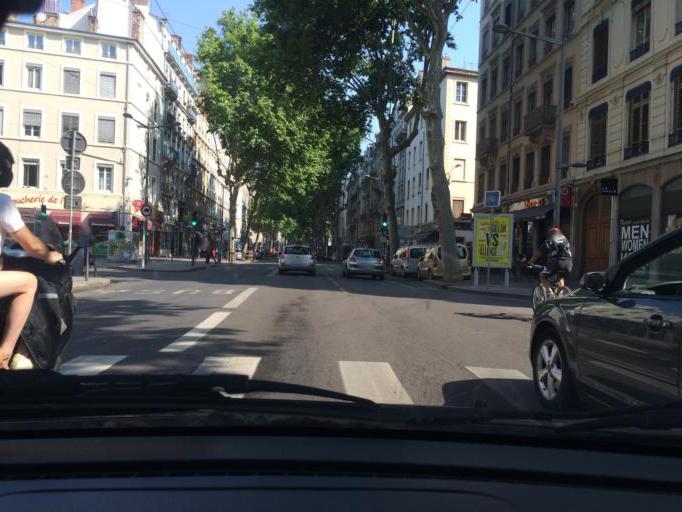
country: FR
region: Rhone-Alpes
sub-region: Departement du Rhone
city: Lyon
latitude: 45.7558
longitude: 4.8466
